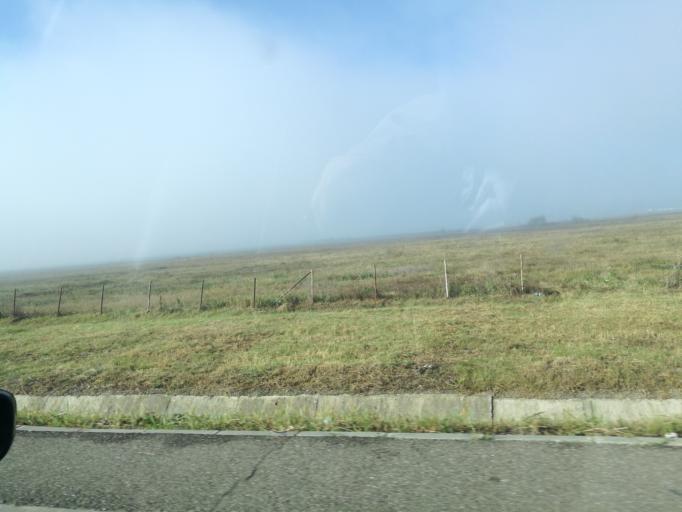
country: RO
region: Iasi
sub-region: Comuna Valea Lupului
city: Valea Lupului
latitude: 47.1685
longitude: 27.5098
